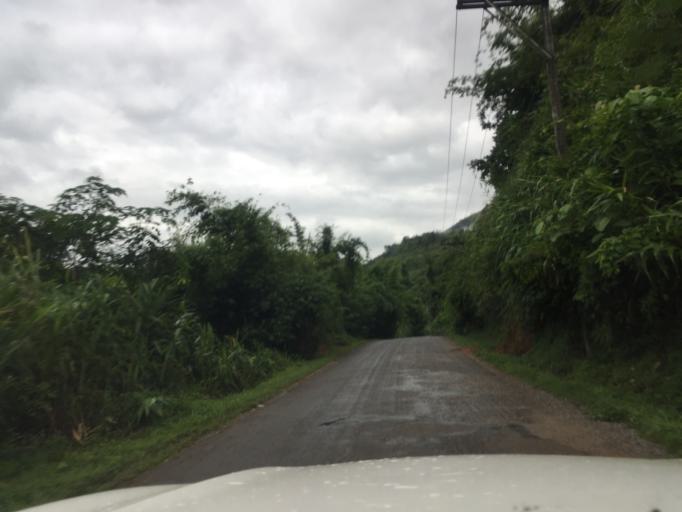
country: LA
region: Oudomxai
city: Muang La
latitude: 20.9456
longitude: 102.2090
